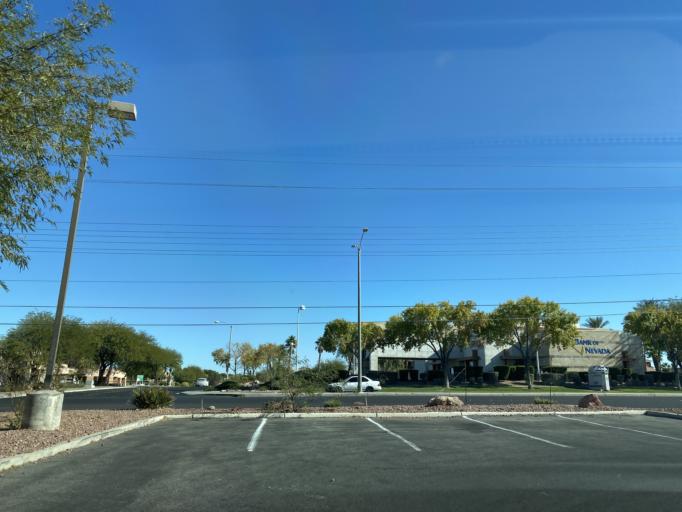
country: US
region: Nevada
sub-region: Clark County
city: Whitney
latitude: 36.0745
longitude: -115.0827
